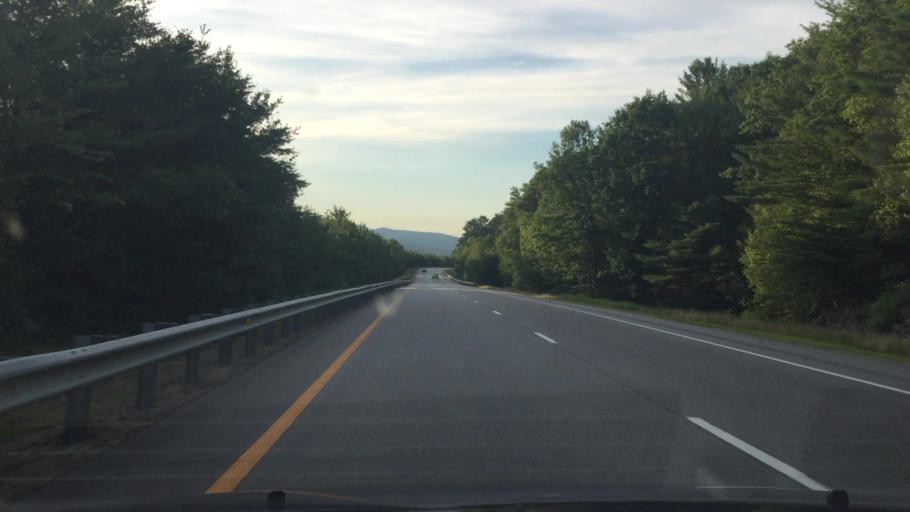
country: US
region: New Hampshire
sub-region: Grafton County
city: Ashland
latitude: 43.7197
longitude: -71.6536
